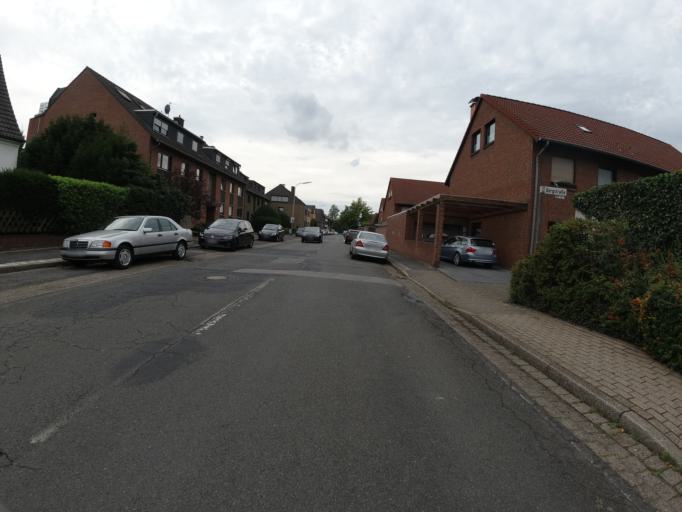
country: DE
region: North Rhine-Westphalia
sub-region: Regierungsbezirk Dusseldorf
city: Moers
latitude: 51.4488
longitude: 6.6475
